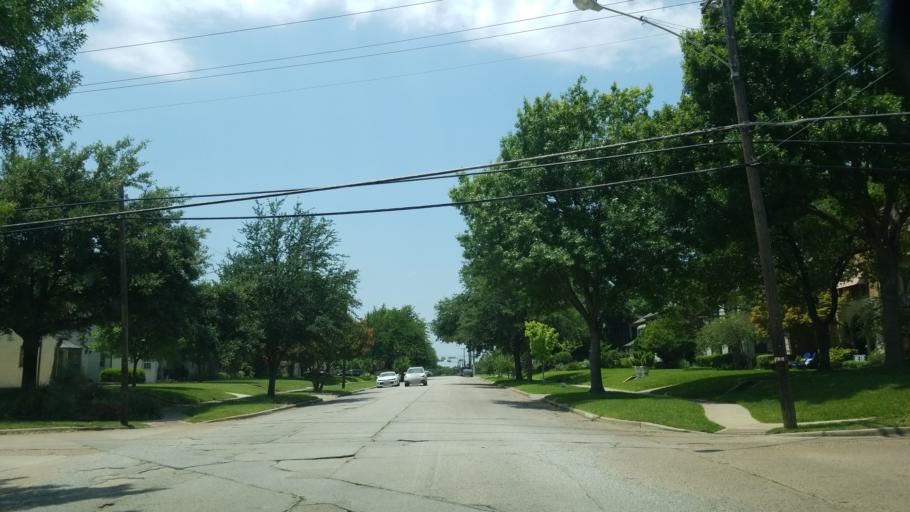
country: US
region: Texas
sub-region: Dallas County
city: Highland Park
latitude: 32.8299
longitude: -96.7656
